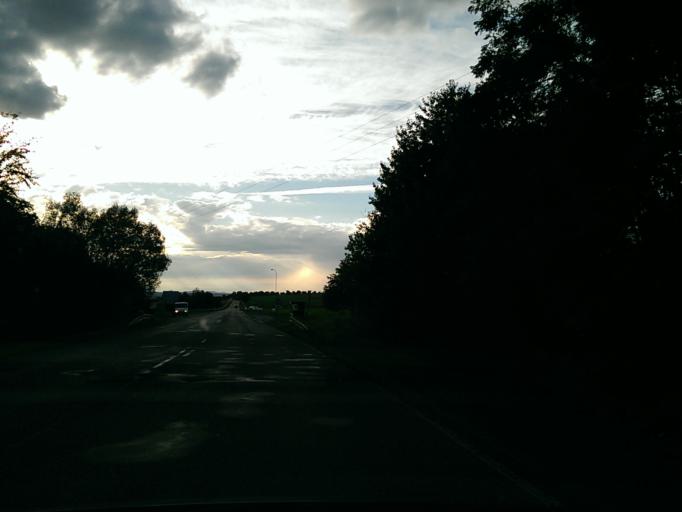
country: CZ
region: Central Bohemia
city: Dolni Bousov
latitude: 50.4642
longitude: 15.1064
